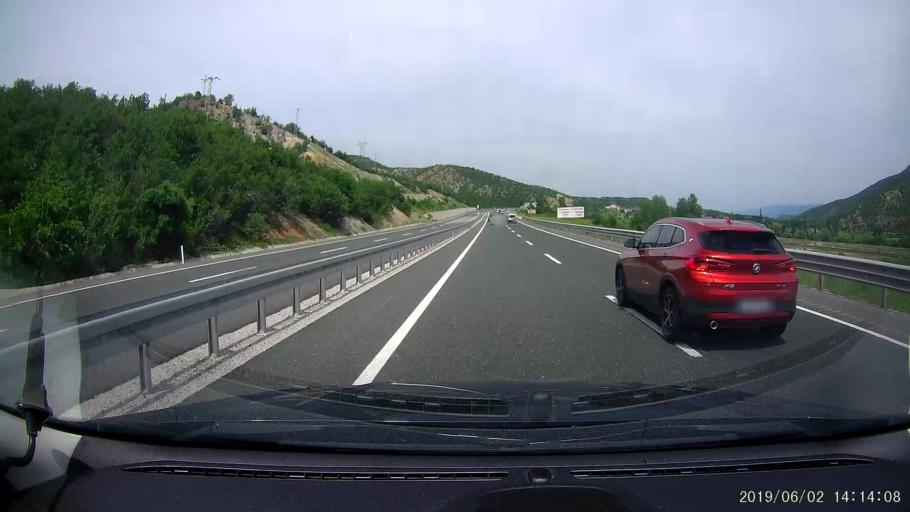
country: TR
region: Cankiri
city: Yaprakli
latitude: 40.9329
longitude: 33.8466
